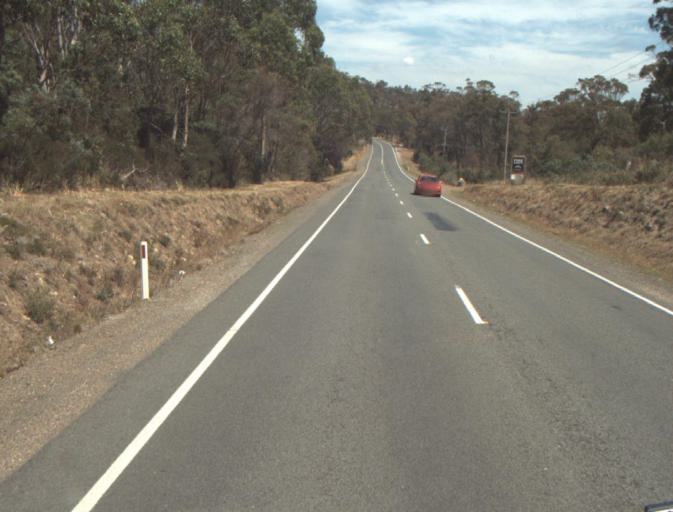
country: AU
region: Tasmania
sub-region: Launceston
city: Mayfield
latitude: -41.3410
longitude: 147.1432
